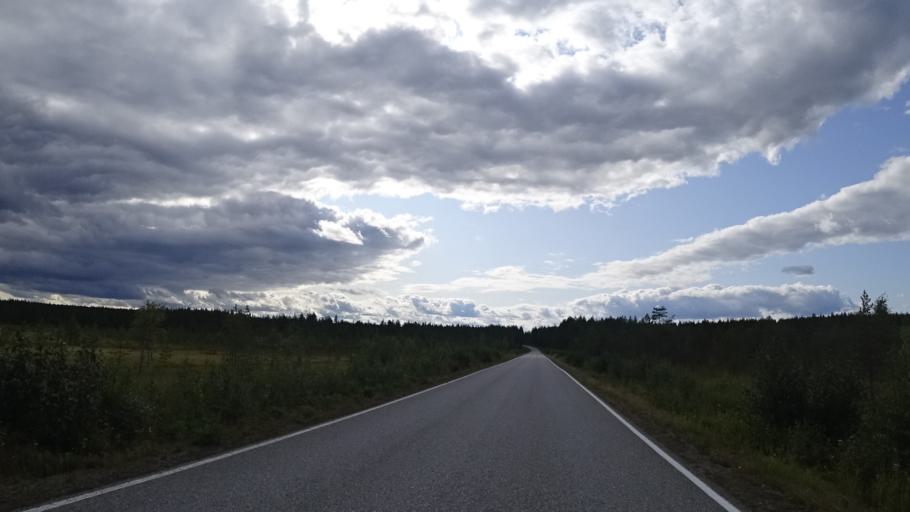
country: FI
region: North Karelia
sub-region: Joensuu
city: Ilomantsi
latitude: 62.4381
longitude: 31.0720
